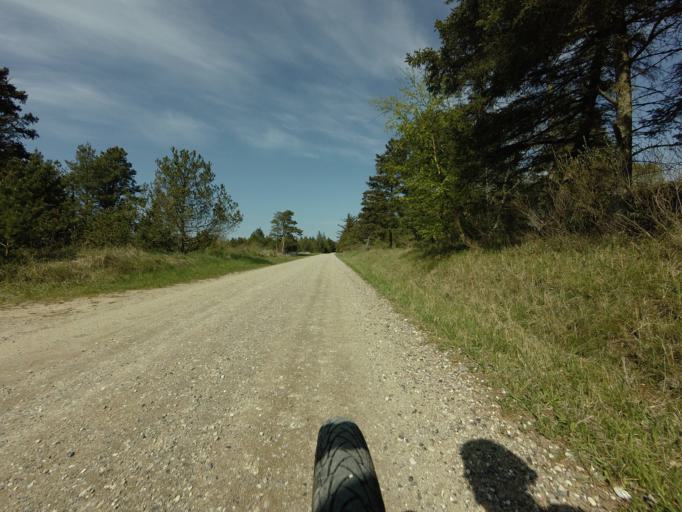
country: DK
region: North Denmark
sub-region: Jammerbugt Kommune
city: Brovst
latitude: 57.2033
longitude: 9.5503
